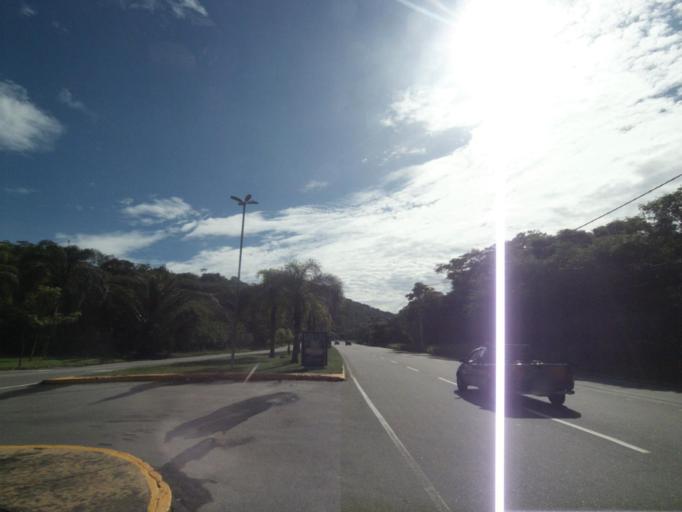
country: BR
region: Rio de Janeiro
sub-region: Niteroi
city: Niteroi
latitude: -22.9272
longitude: -43.0626
